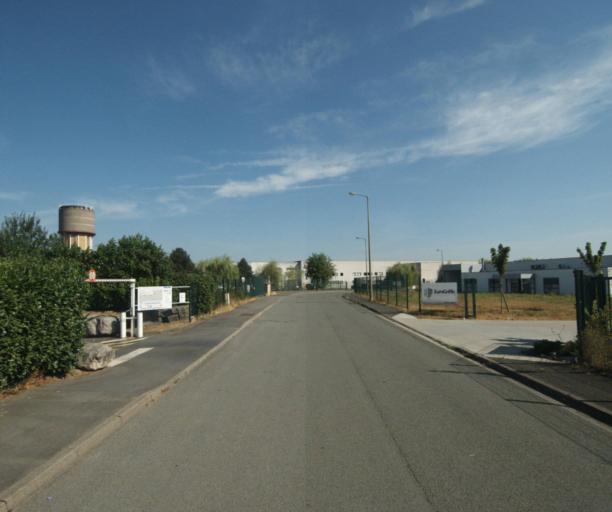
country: FR
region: Nord-Pas-de-Calais
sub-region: Departement du Nord
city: Halluin
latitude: 50.7873
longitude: 3.1422
